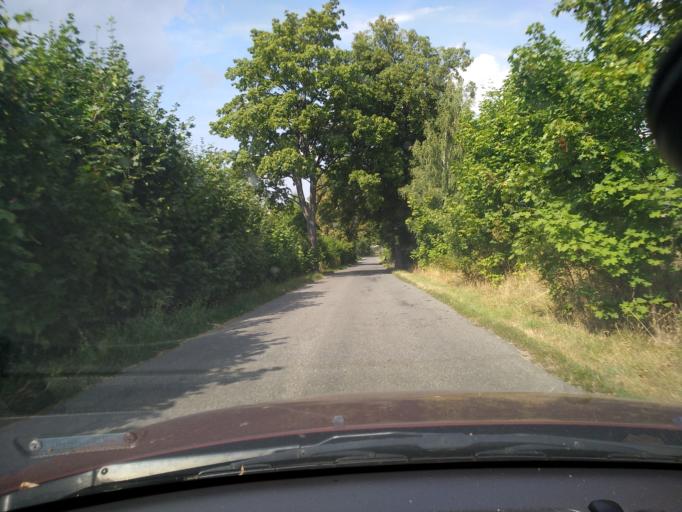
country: PL
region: Lower Silesian Voivodeship
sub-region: Powiat jeleniogorski
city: Stara Kamienica
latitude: 50.8843
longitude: 15.5509
